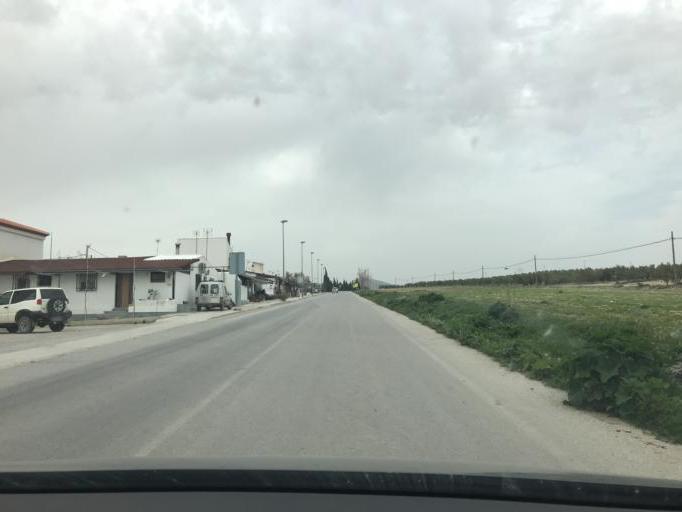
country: ES
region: Andalusia
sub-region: Provincia de Granada
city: Castril
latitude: 37.7677
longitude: -2.7558
